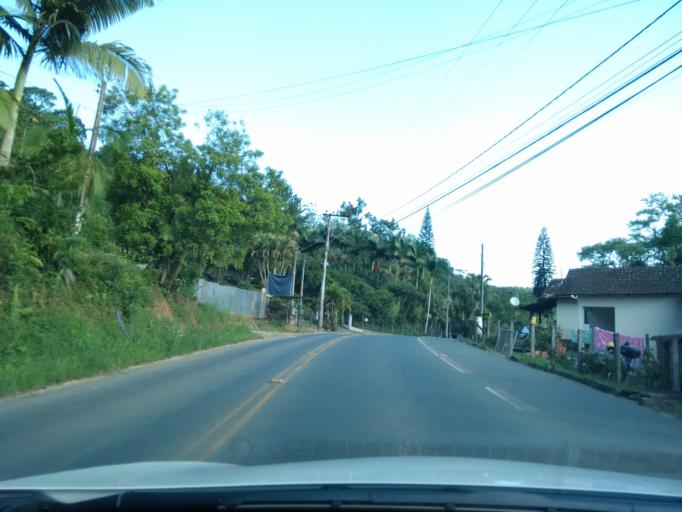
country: BR
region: Santa Catarina
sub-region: Blumenau
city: Blumenau
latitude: -26.8559
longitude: -49.0767
